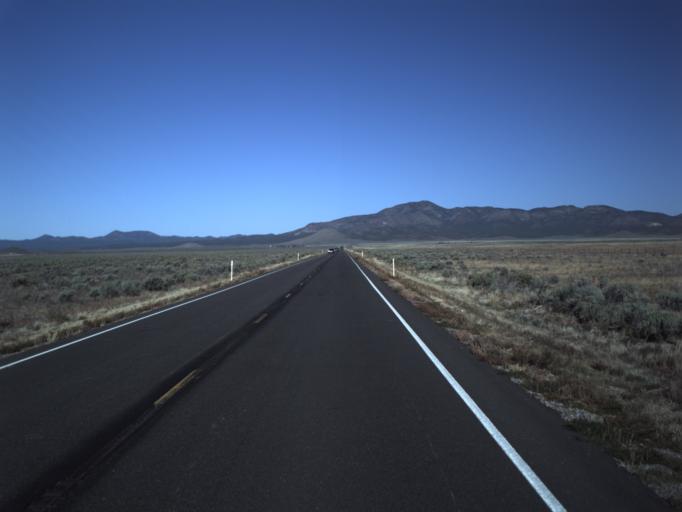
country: US
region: Utah
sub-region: Washington County
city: Enterprise
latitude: 37.7776
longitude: -113.8500
